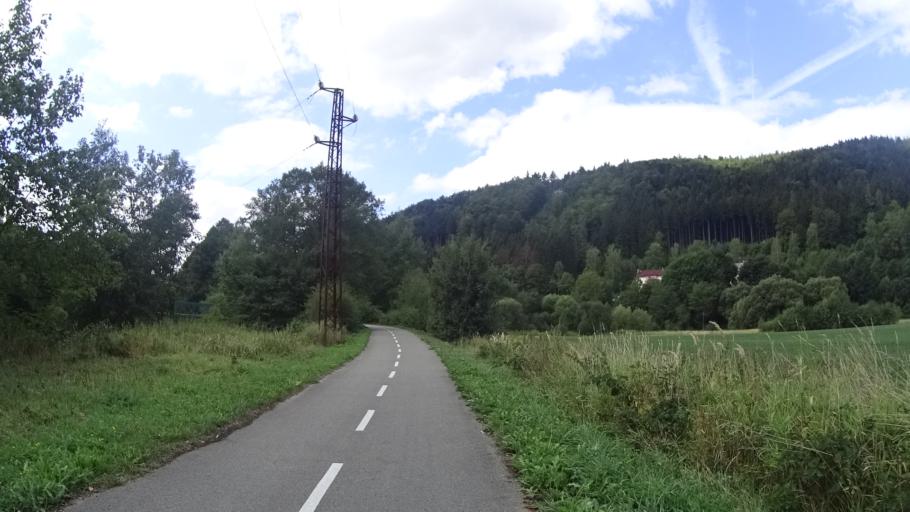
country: CZ
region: Pardubicky
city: Dolni Dobrouc
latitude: 49.9984
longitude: 16.4520
